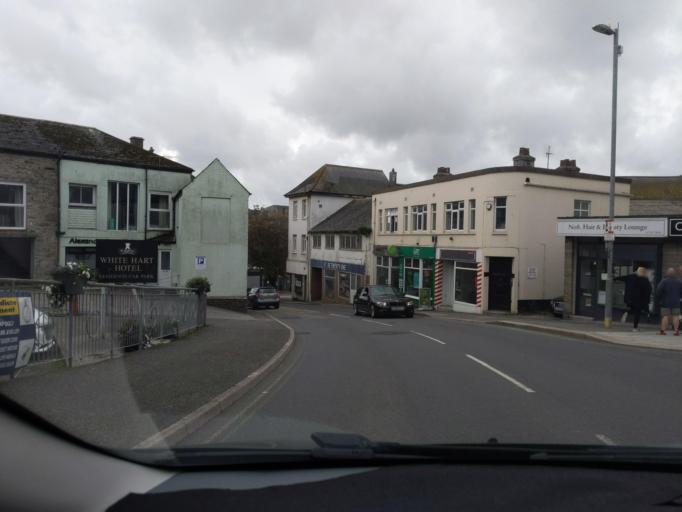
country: GB
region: England
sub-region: Cornwall
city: St Austell
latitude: 50.3378
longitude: -4.7912
